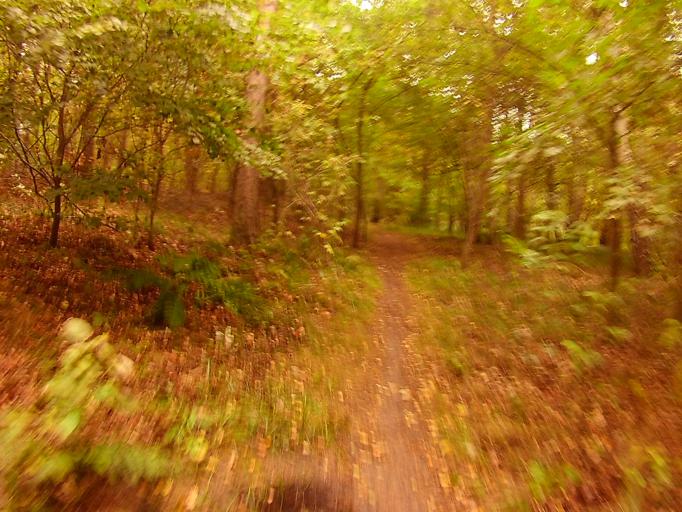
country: DE
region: Berlin
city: Grunau
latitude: 52.4045
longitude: 13.6084
